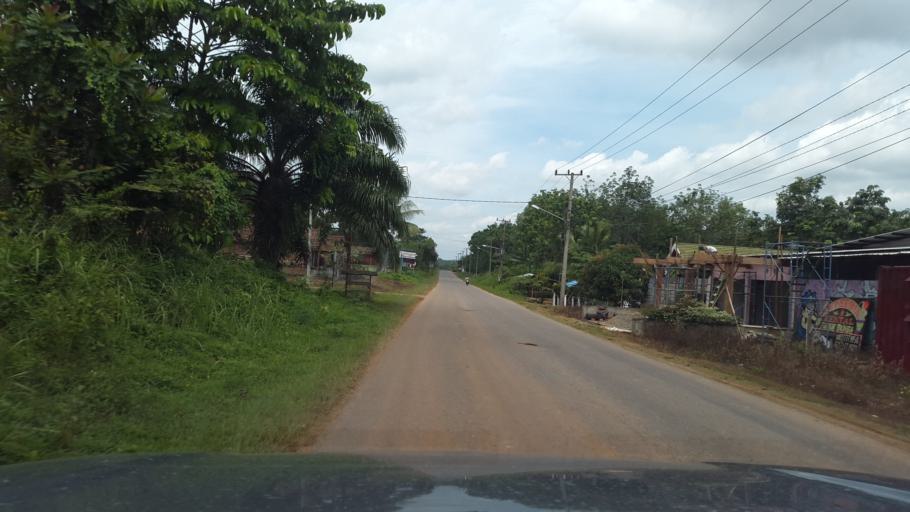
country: ID
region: South Sumatra
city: Gunungmegang Dalam
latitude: -3.3268
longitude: 103.9048
